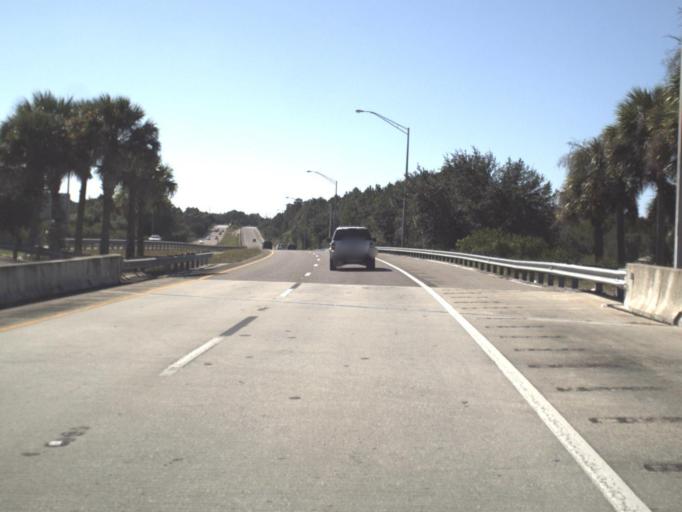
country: US
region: Florida
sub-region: Hillsborough County
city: Cheval
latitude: 28.1326
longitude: -82.5224
